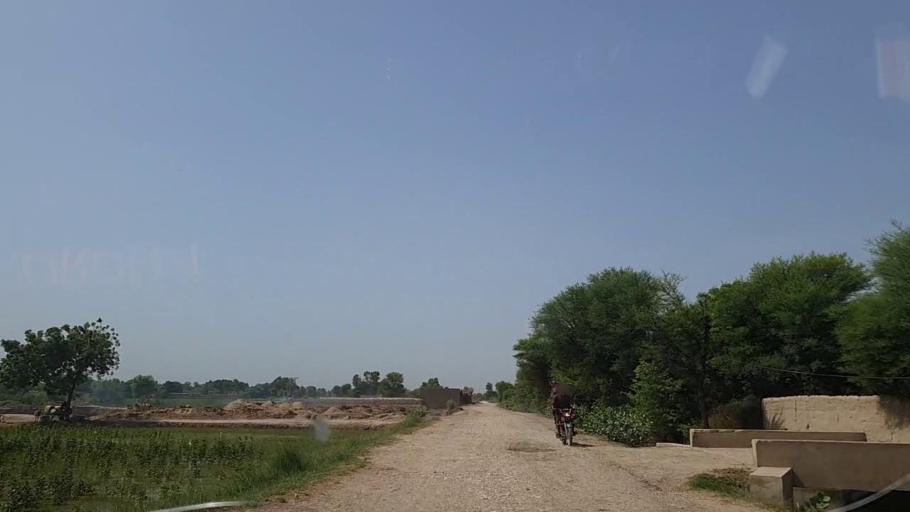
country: PK
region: Sindh
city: Naushahro Firoz
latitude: 26.8569
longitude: 68.0290
